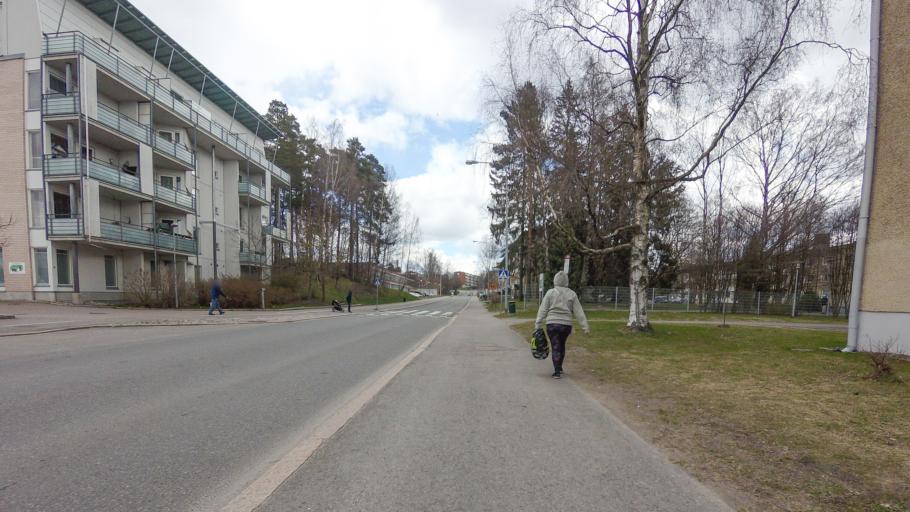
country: FI
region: Uusimaa
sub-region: Helsinki
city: Vantaa
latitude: 60.2126
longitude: 25.0971
